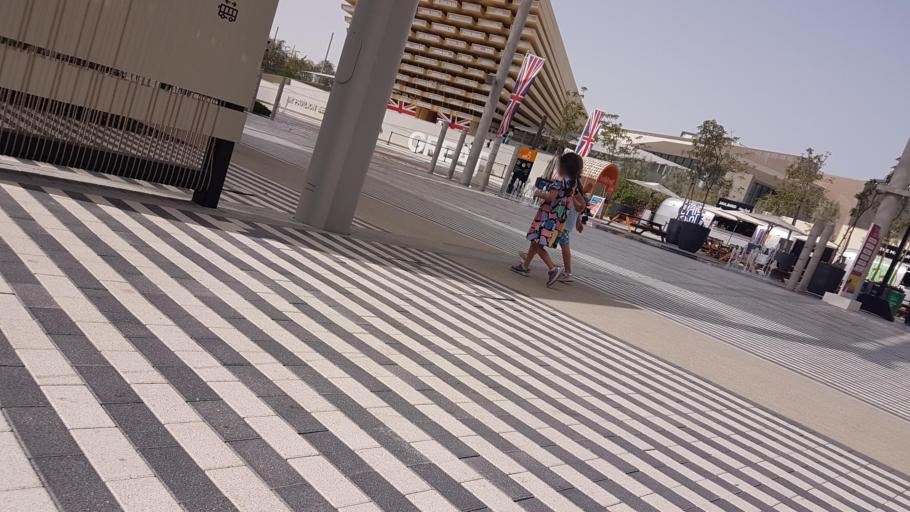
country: AE
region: Dubai
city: Dubai
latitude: 24.9641
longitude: 55.1508
